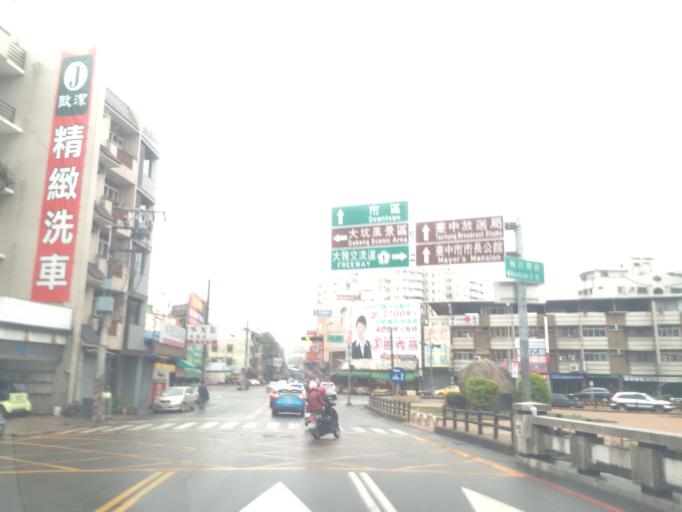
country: TW
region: Taiwan
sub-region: Taichung City
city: Taichung
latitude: 24.1826
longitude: 120.6881
